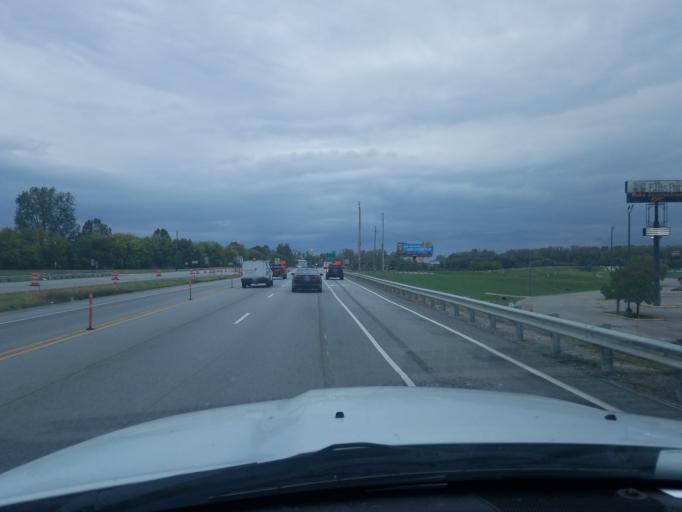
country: US
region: Indiana
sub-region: Vanderburgh County
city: Evansville
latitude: 37.9149
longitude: -87.5483
